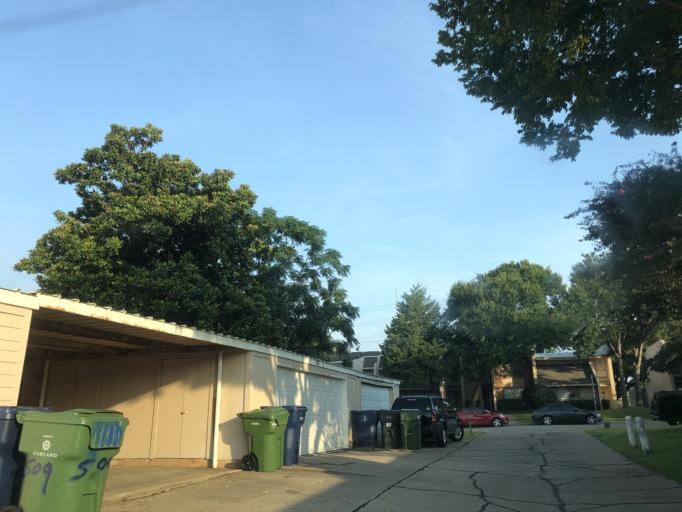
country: US
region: Texas
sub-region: Dallas County
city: Garland
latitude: 32.8652
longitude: -96.6361
